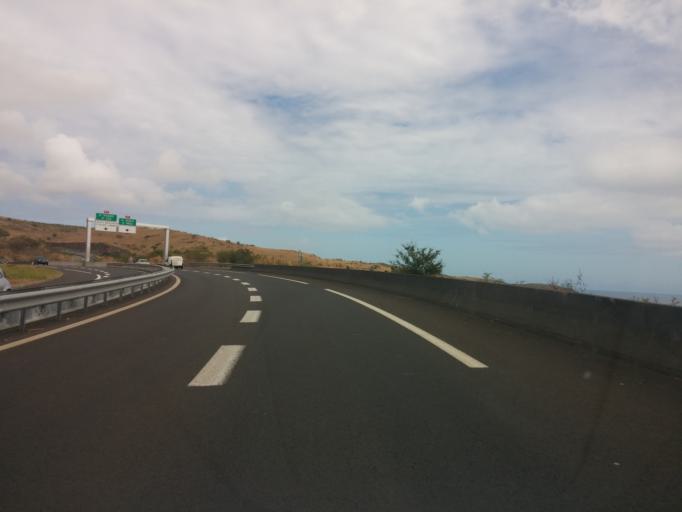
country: RE
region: Reunion
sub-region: Reunion
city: Saint-Paul
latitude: -21.0196
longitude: 55.2587
